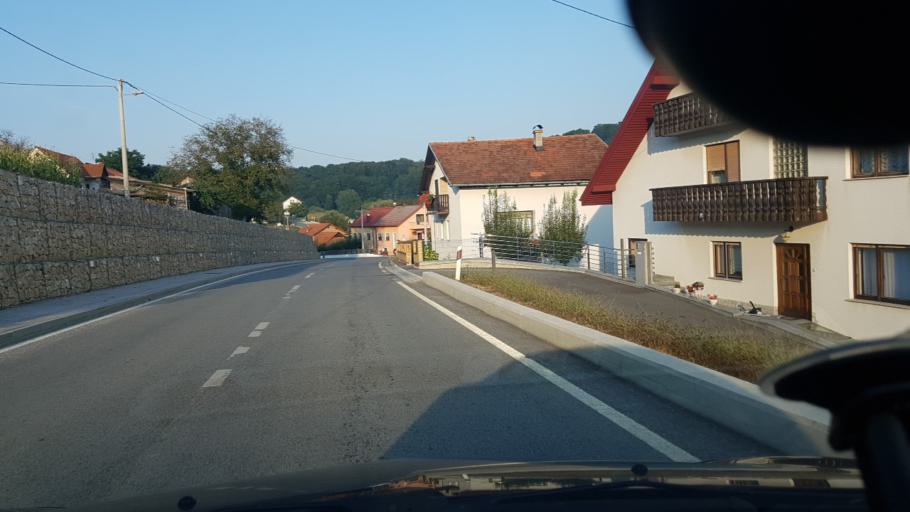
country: HR
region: Krapinsko-Zagorska
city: Pregrada
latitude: 46.1556
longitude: 15.8099
